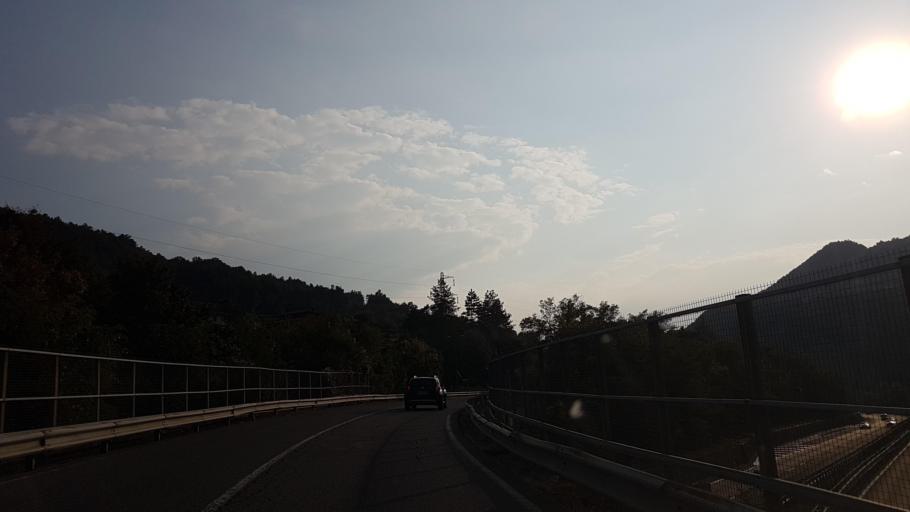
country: IT
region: Emilia-Romagna
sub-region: Provincia di Parma
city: Solignano
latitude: 44.6238
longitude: 10.0070
